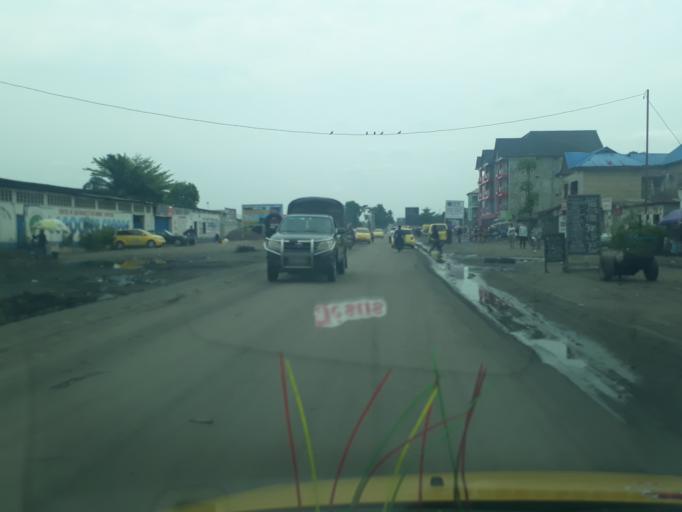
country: CD
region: Kinshasa
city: Kinshasa
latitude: -4.3469
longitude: 15.3021
